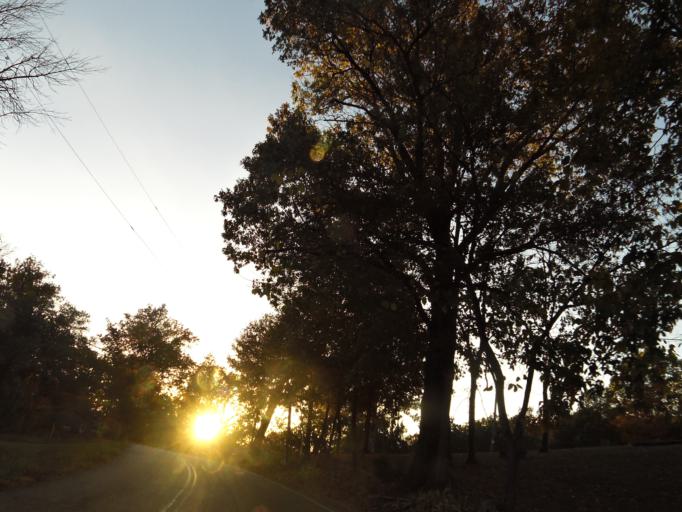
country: US
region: Tennessee
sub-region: Sevier County
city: Seymour
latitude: 35.9295
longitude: -83.7389
